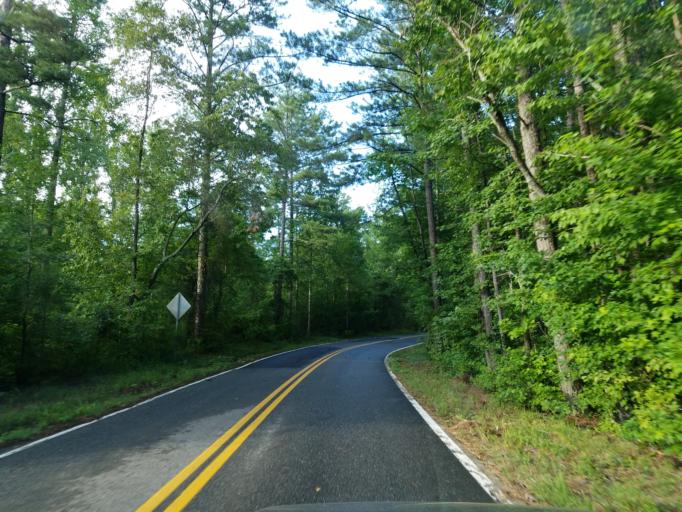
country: US
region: Georgia
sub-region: Bartow County
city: Rydal
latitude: 34.2186
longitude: -84.6368
